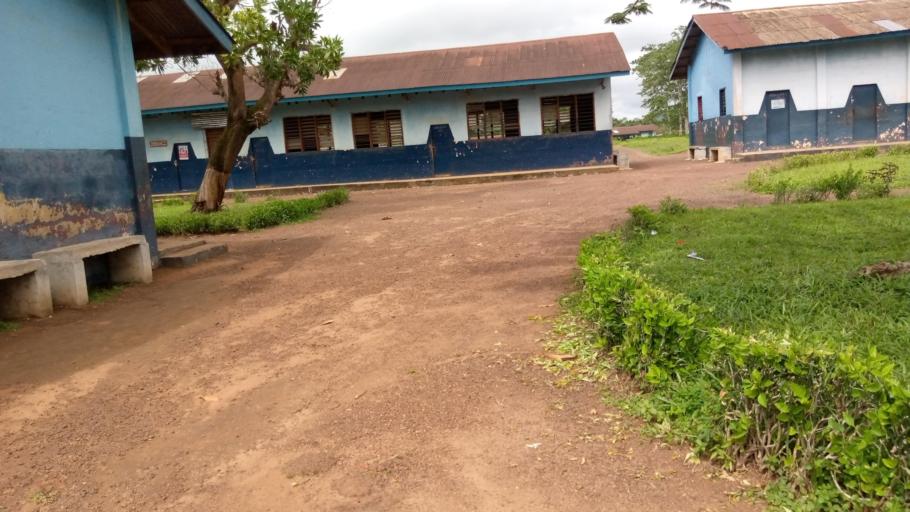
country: SL
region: Southern Province
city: Moyamba
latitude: 8.1526
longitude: -12.4310
